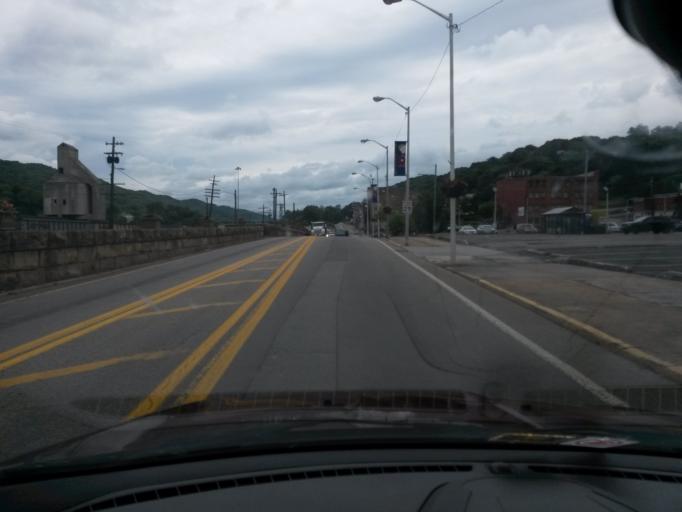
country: US
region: West Virginia
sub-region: Mercer County
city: Bluefield
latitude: 37.2699
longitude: -81.2226
